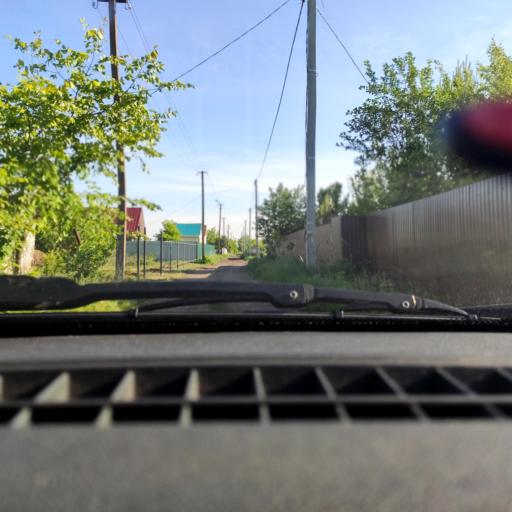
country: RU
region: Bashkortostan
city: Avdon
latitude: 54.4653
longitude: 55.8203
